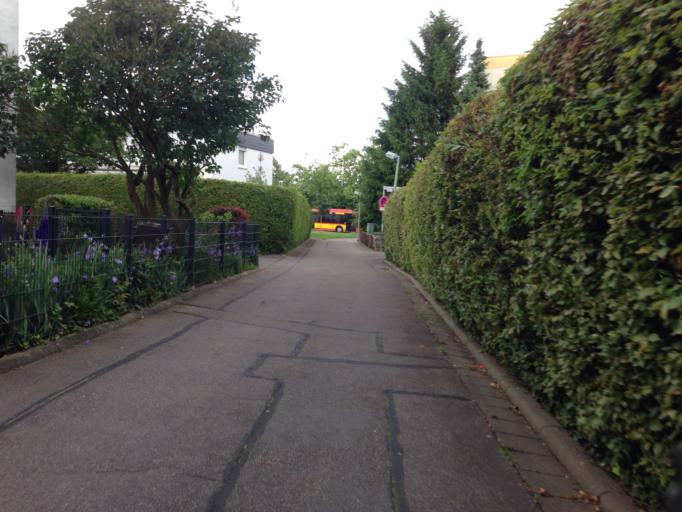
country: DE
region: Hesse
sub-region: Regierungsbezirk Darmstadt
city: Hanau am Main
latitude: 50.1343
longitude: 8.8862
